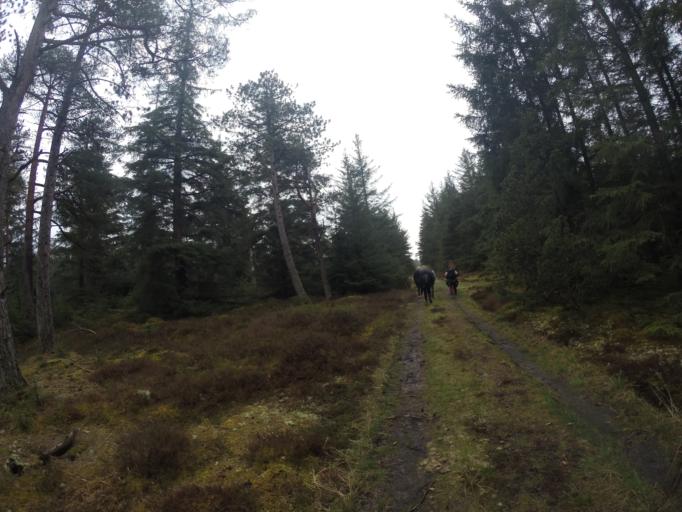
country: DK
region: North Denmark
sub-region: Thisted Kommune
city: Hanstholm
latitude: 57.0420
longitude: 8.5720
